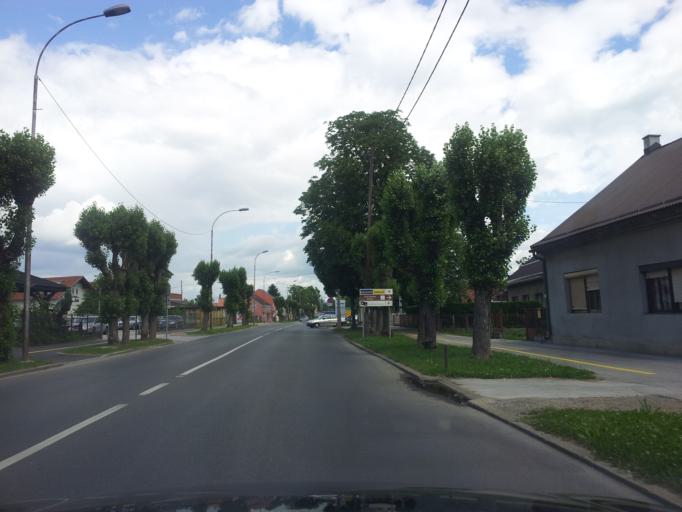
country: HR
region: Karlovacka
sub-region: Grad Karlovac
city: Karlovac
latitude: 45.5079
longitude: 15.5487
